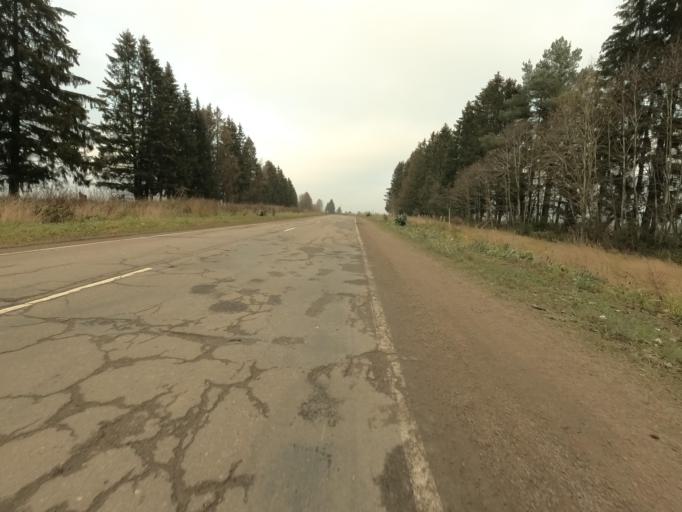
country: RU
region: Leningrad
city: Mga
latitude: 59.7798
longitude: 31.0248
